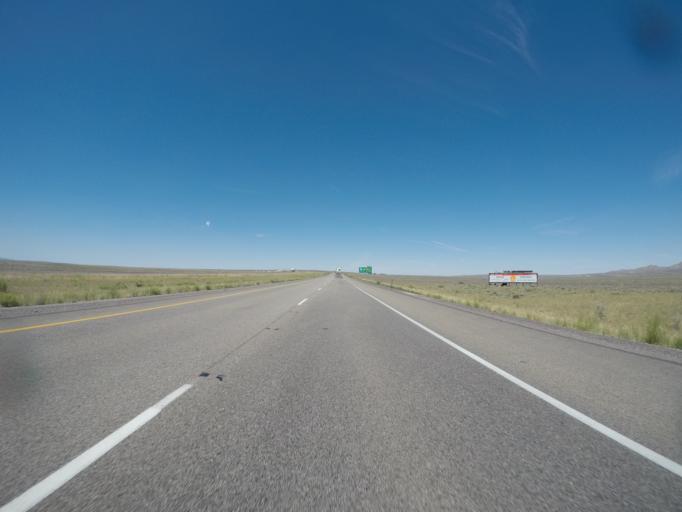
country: US
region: Wyoming
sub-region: Carbon County
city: Saratoga
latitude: 41.7423
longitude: -106.7993
